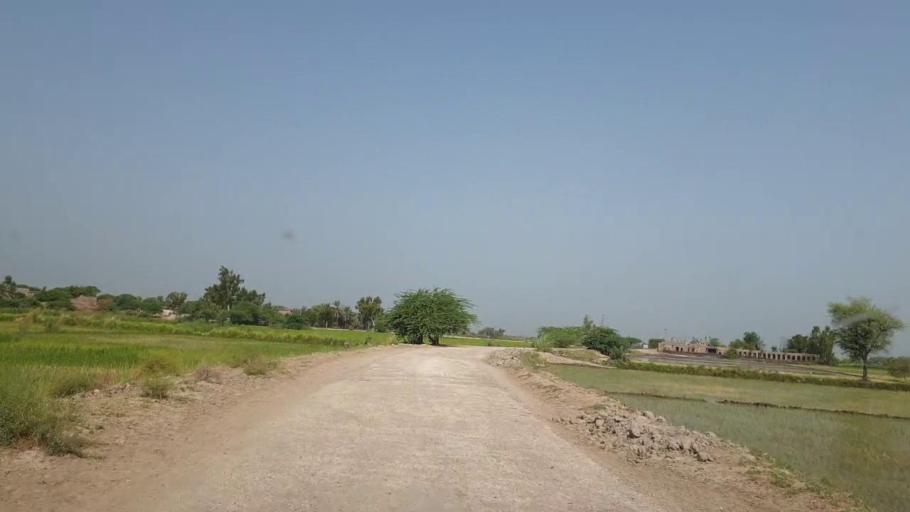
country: PK
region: Sindh
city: Lakhi
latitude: 27.8281
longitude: 68.6869
